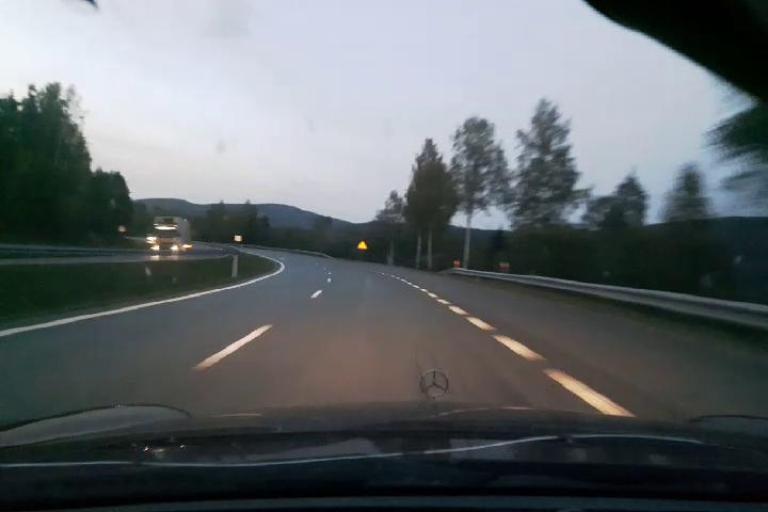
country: SE
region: Vaesternorrland
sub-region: Kramfors Kommun
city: Nordingra
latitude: 63.0122
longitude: 18.2906
